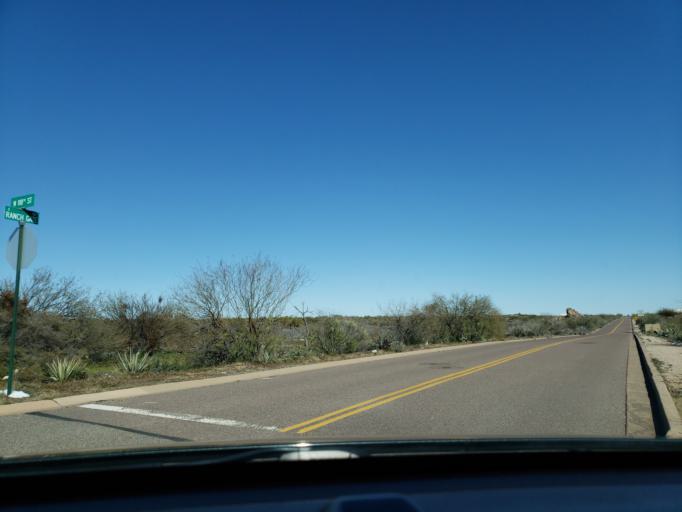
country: US
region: Arizona
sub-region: Maricopa County
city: Carefree
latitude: 33.7162
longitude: -111.8263
